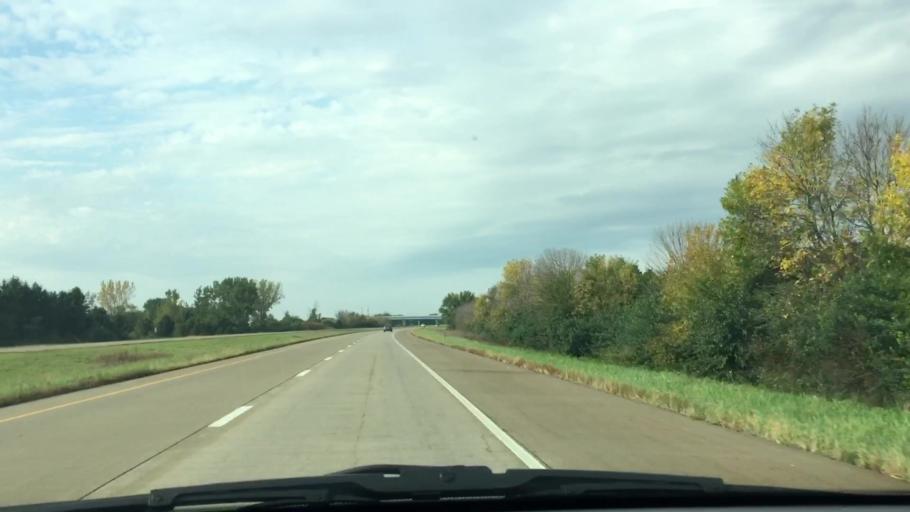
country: US
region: Illinois
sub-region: Whiteside County
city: Prophetstown
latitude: 41.7563
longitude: -89.8563
